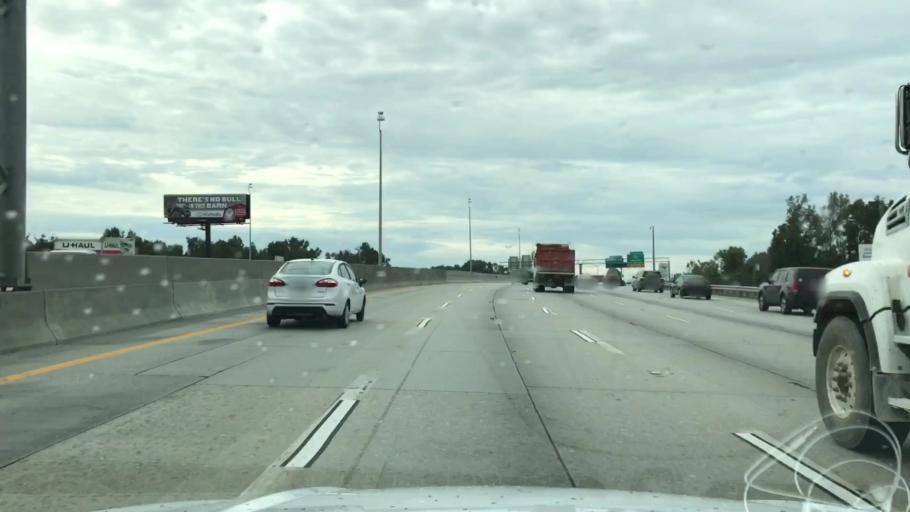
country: US
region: South Carolina
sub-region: Berkeley County
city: Hanahan
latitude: 32.8941
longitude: -80.0187
